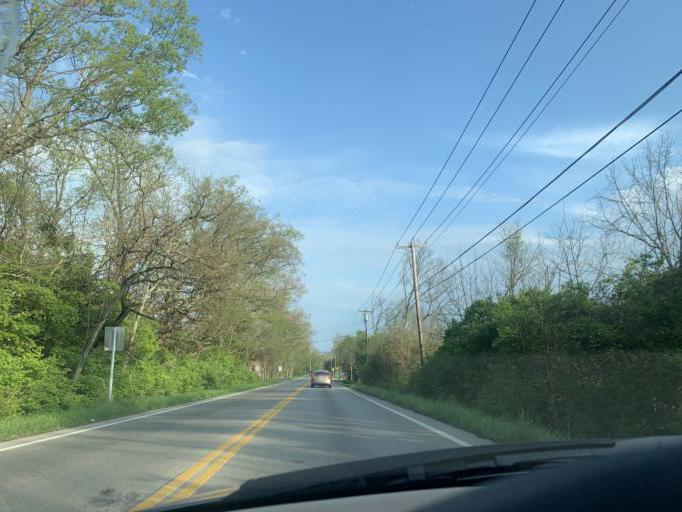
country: US
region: Ohio
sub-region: Hamilton County
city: Glendale
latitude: 39.2676
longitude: -84.4720
